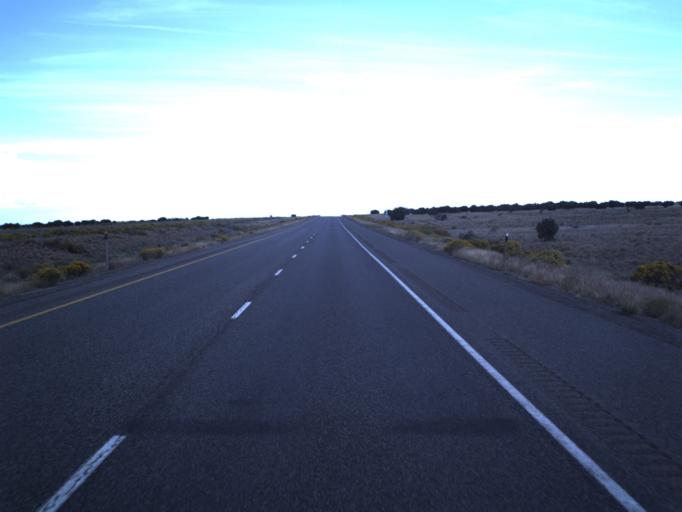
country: US
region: Utah
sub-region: Emery County
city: Castle Dale
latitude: 38.8939
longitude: -110.6191
